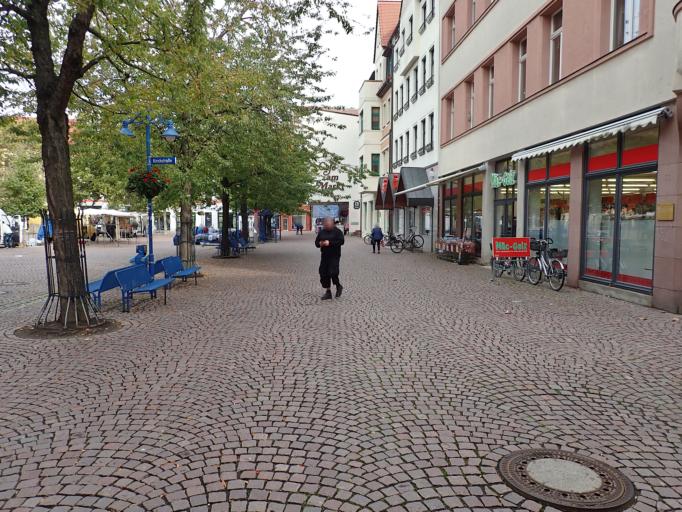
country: DE
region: Saxony
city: Bitterfeld-Wolfen
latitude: 51.6234
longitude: 12.3298
